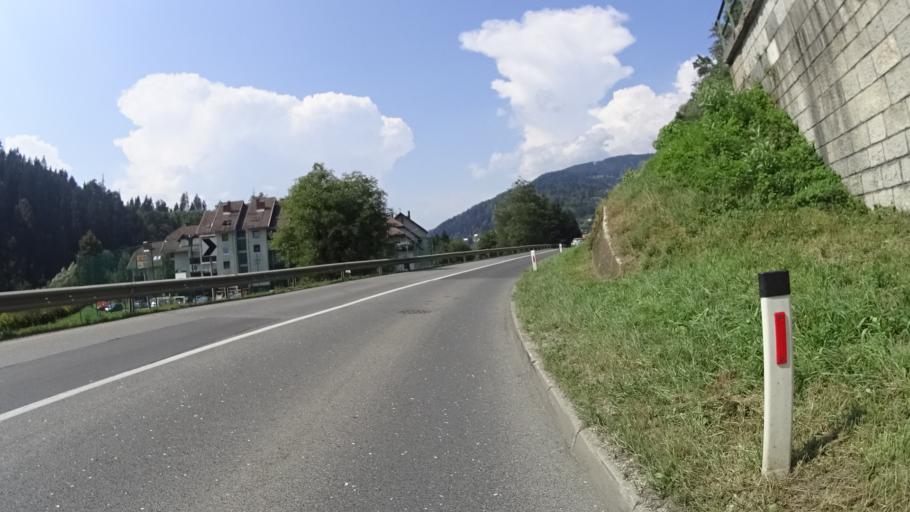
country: SI
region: Dravograd
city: Dravograd
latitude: 46.5808
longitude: 15.0241
